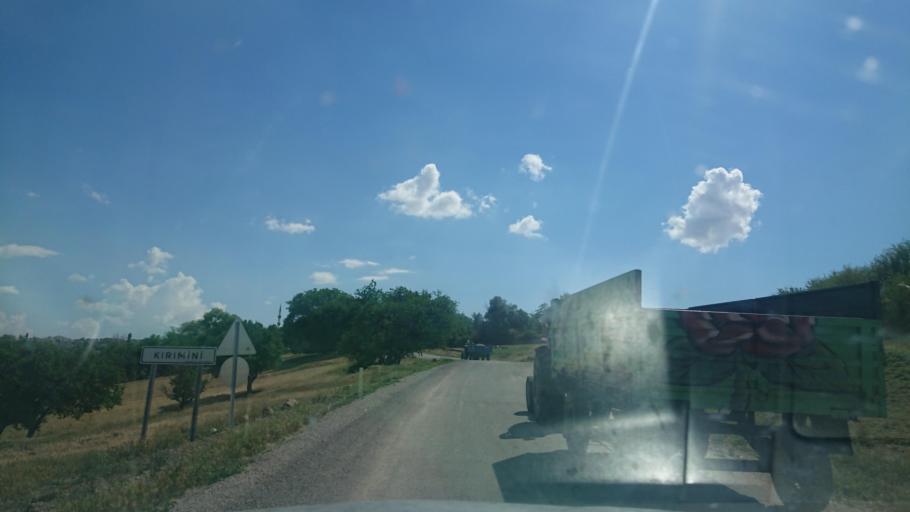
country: TR
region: Aksaray
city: Agacoren
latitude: 38.7752
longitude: 33.7879
